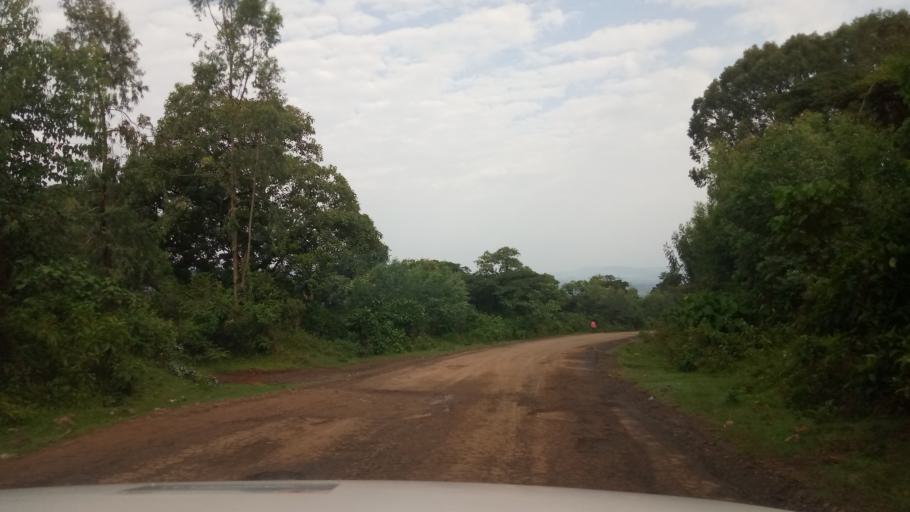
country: ET
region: Oromiya
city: Agaro
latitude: 7.7974
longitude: 36.7184
